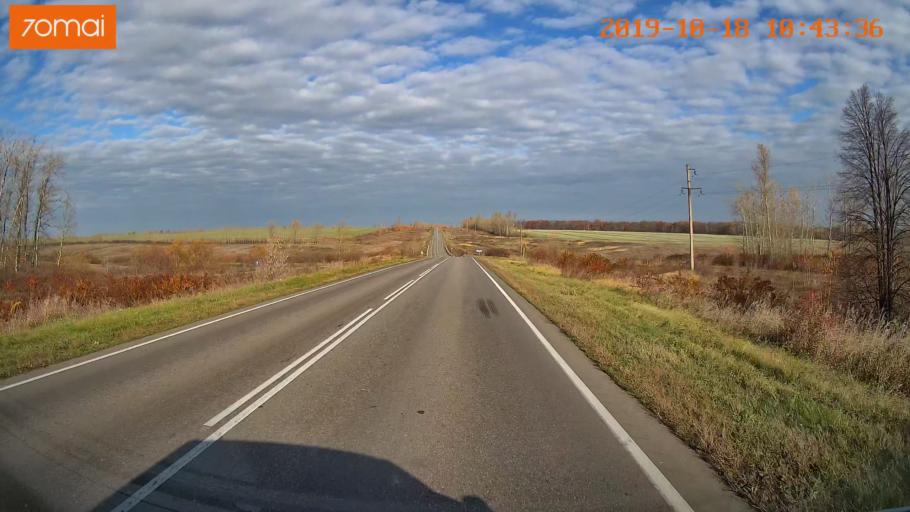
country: RU
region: Tula
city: Kurkino
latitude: 53.6416
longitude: 38.6839
